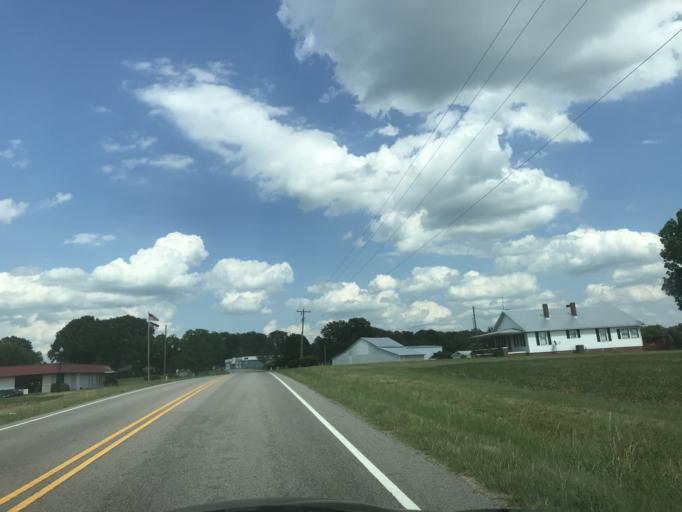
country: US
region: North Carolina
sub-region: Wake County
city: Zebulon
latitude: 35.9591
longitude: -78.2597
